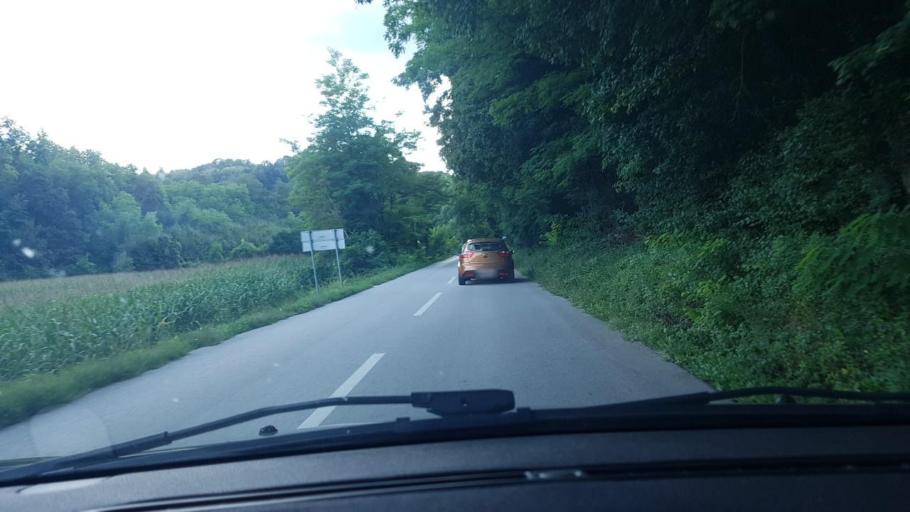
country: HR
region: Krapinsko-Zagorska
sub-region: Grad Krapina
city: Krapina
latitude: 46.1022
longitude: 15.8657
